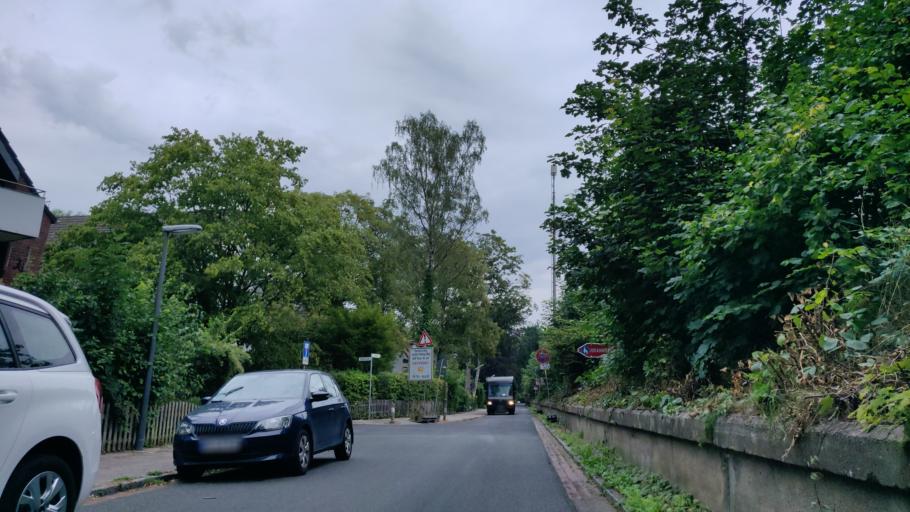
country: DE
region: Lower Saxony
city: Lilienthal
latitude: 53.0978
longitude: 8.8771
